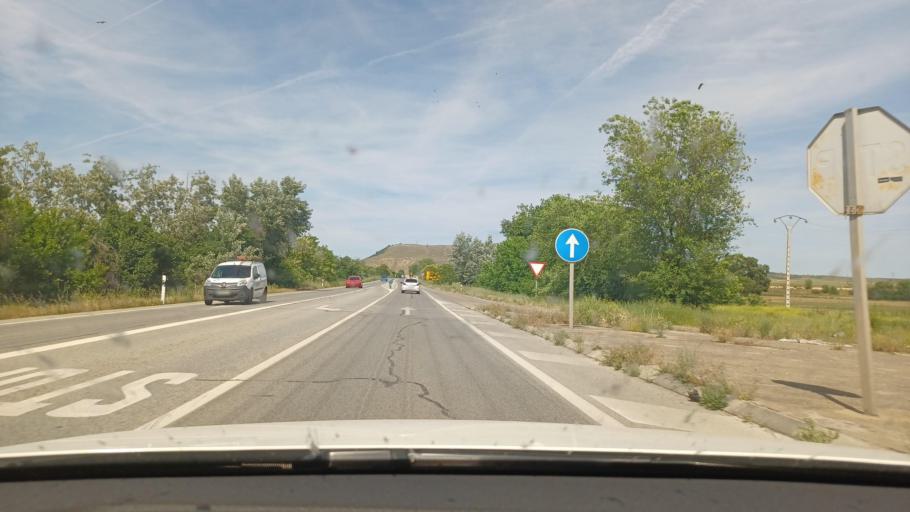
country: ES
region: Madrid
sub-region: Provincia de Madrid
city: Torrejon de Ardoz
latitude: 40.4330
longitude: -3.4394
